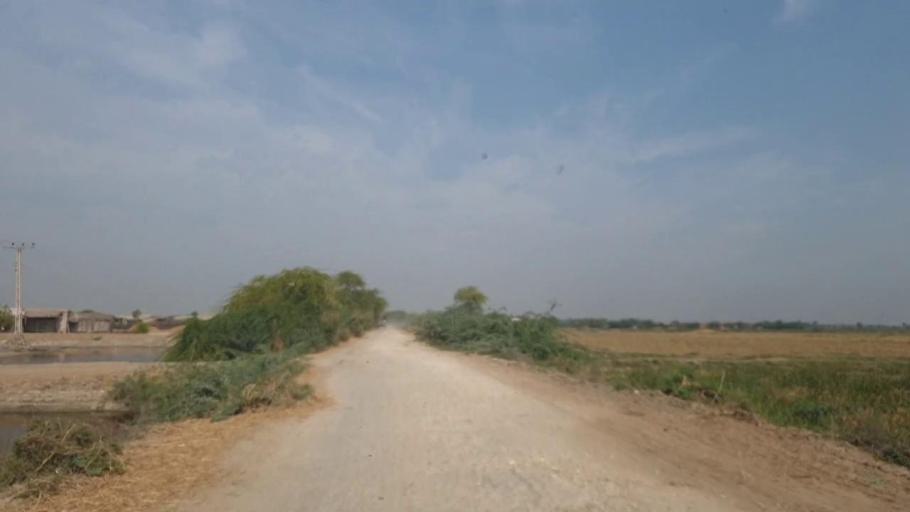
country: PK
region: Sindh
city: Tando Bago
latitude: 24.9103
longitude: 68.9963
